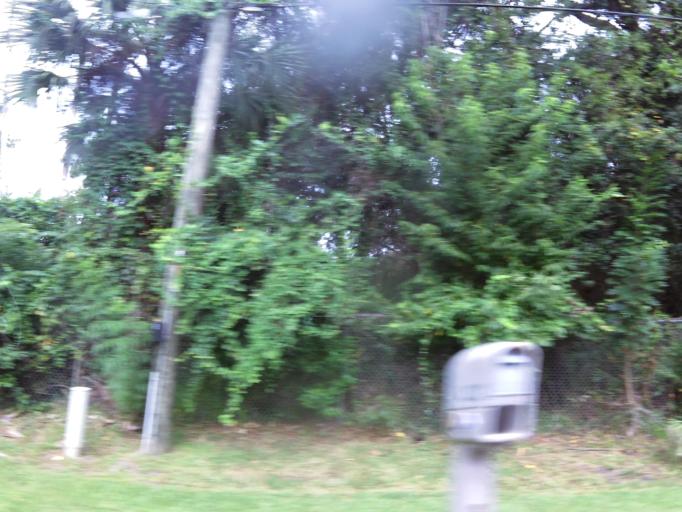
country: US
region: Florida
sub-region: Clay County
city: Bellair-Meadowbrook Terrace
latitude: 30.2593
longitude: -81.7260
